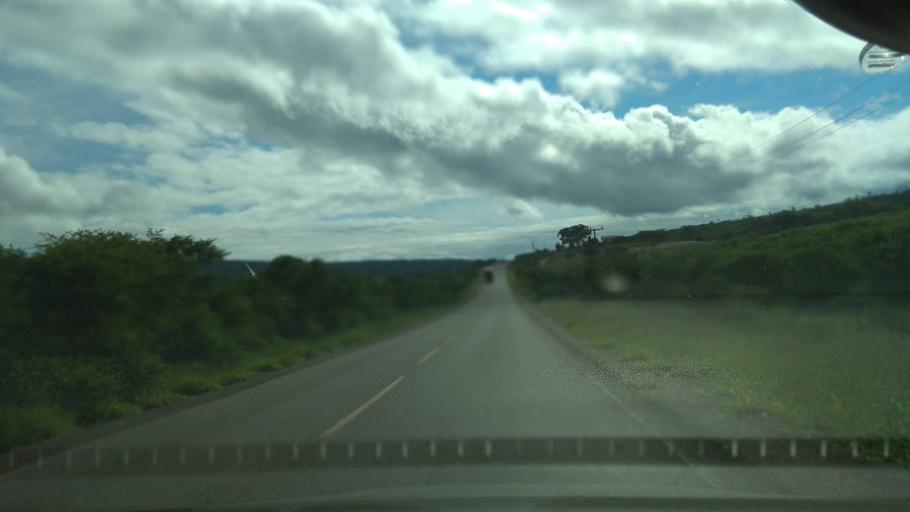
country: BR
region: Bahia
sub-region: Jaguaquara
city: Jaguaquara
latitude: -13.4366
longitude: -39.9304
